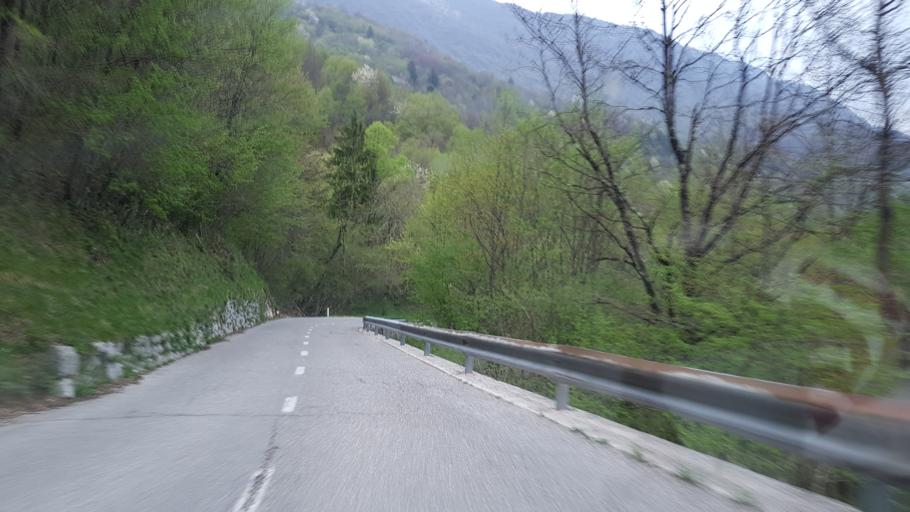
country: SI
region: Kobarid
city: Kobarid
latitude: 46.2548
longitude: 13.4972
